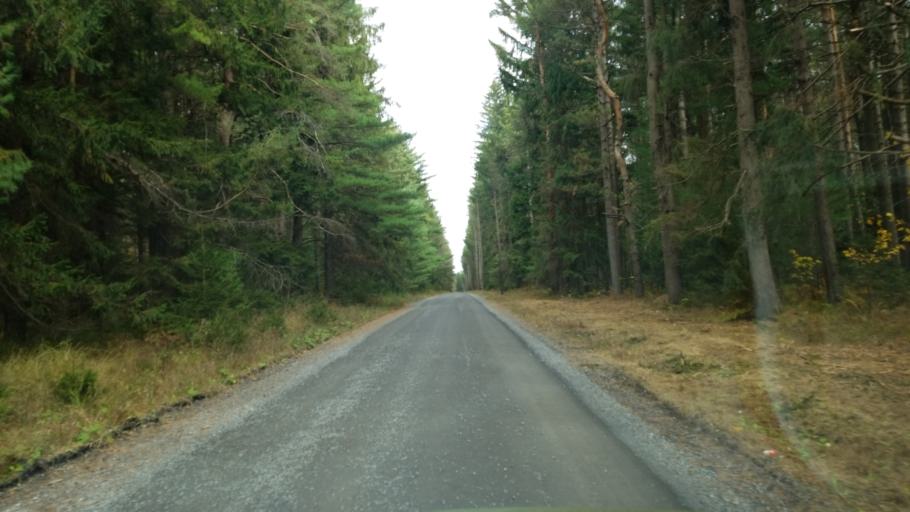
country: US
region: Pennsylvania
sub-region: Clearfield County
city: Clearfield
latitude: 41.1949
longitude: -78.4370
